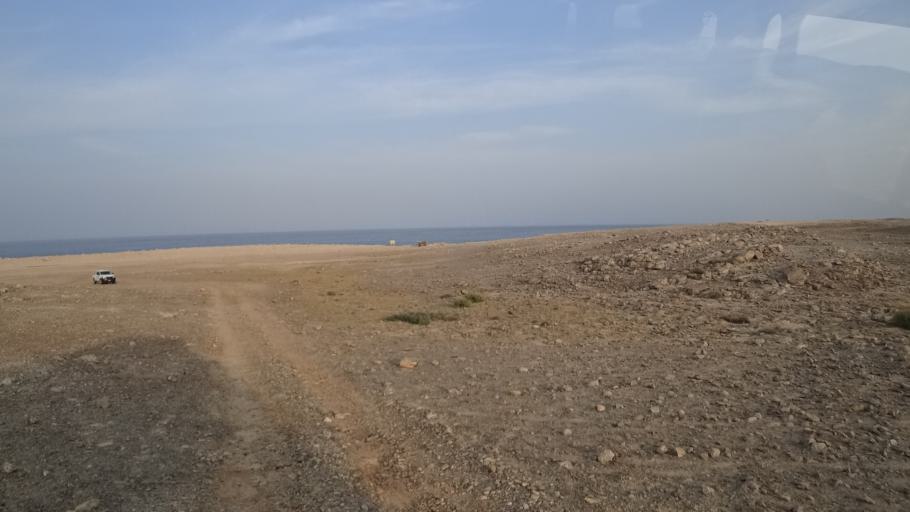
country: OM
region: Ash Sharqiyah
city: Sur
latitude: 22.4572
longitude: 59.8266
